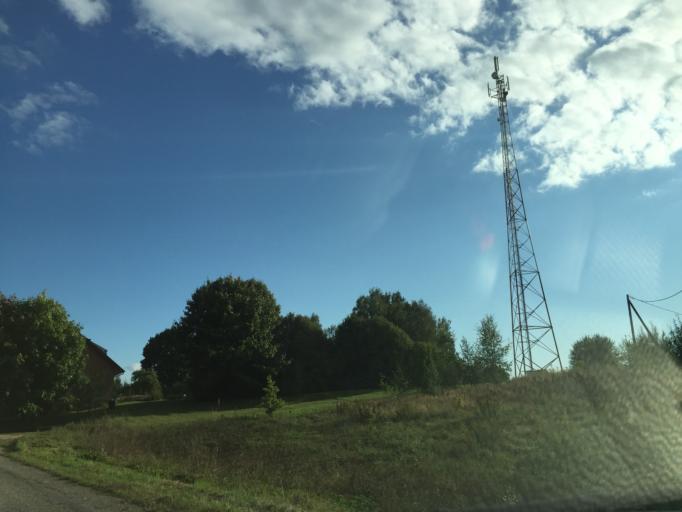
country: LV
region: Krimulda
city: Ragana
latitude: 57.2554
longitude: 24.6710
